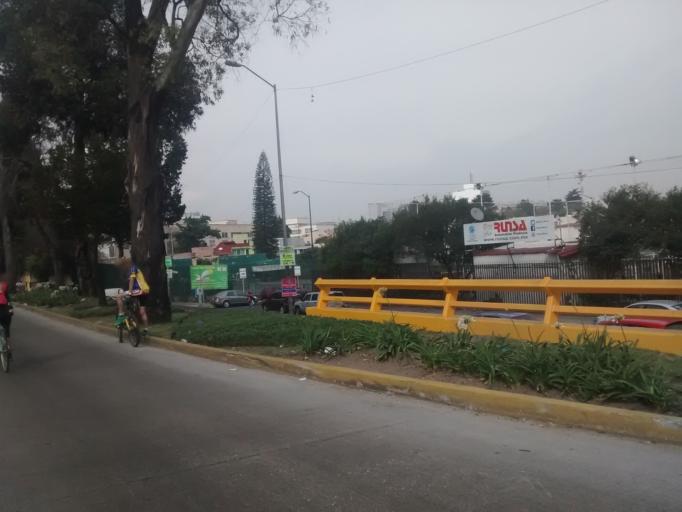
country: MX
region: Mexico City
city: Coyoacan
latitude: 19.3579
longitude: -99.1556
